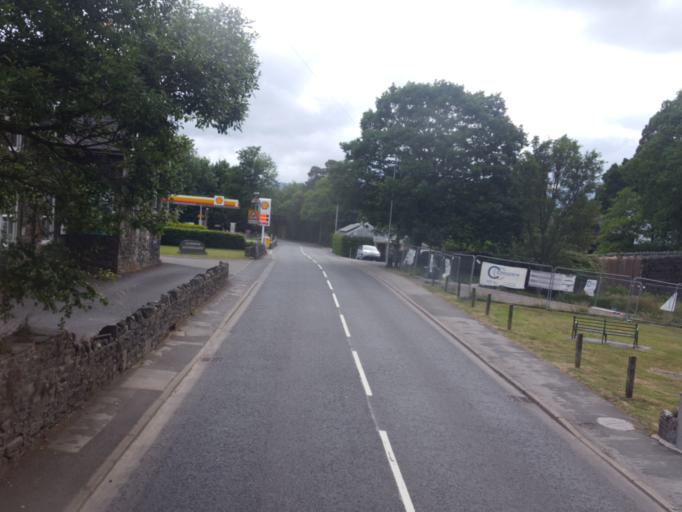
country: GB
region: England
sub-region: Cumbria
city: Keswick
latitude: 54.6045
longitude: -3.1236
